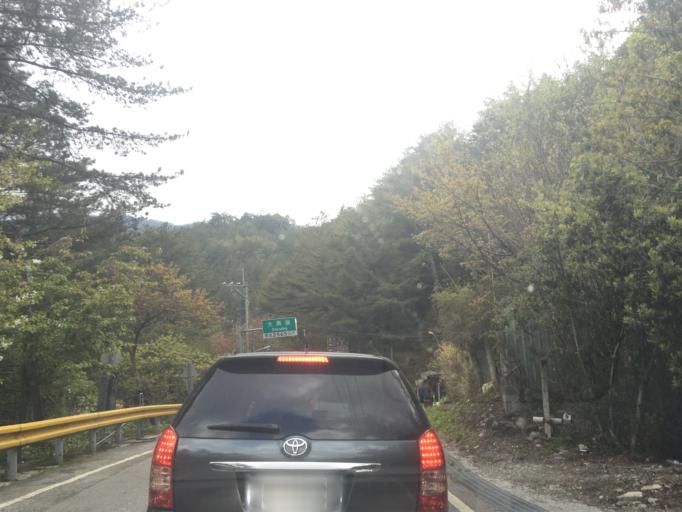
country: TW
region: Taiwan
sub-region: Hualien
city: Hualian
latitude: 24.1804
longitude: 121.3115
